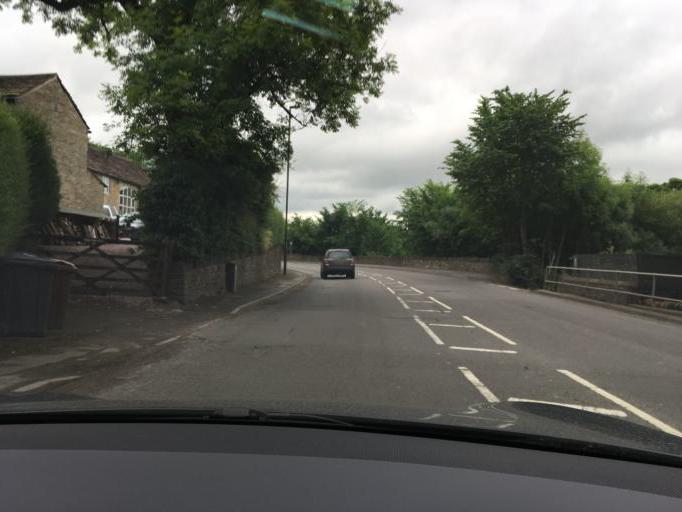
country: GB
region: England
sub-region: Derbyshire
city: New Mills
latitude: 53.3562
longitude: -1.9992
